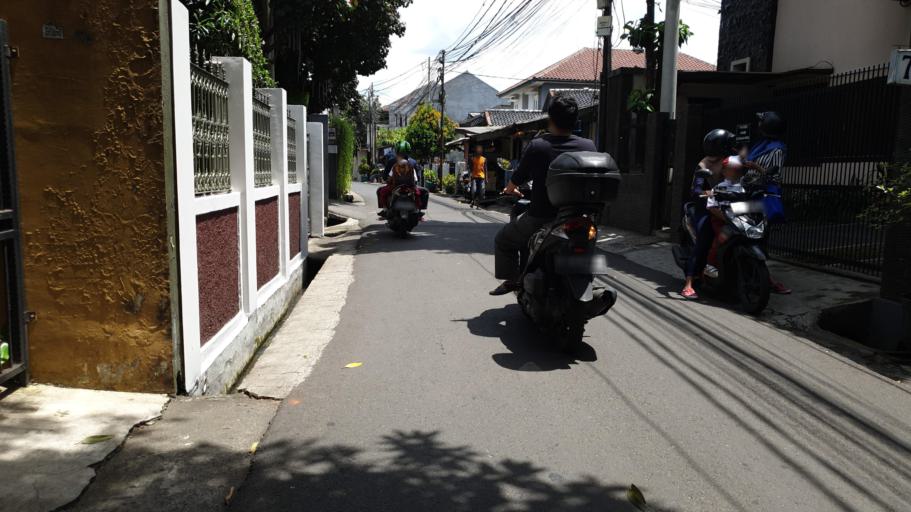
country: ID
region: Banten
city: South Tangerang
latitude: -6.2656
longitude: 106.7888
